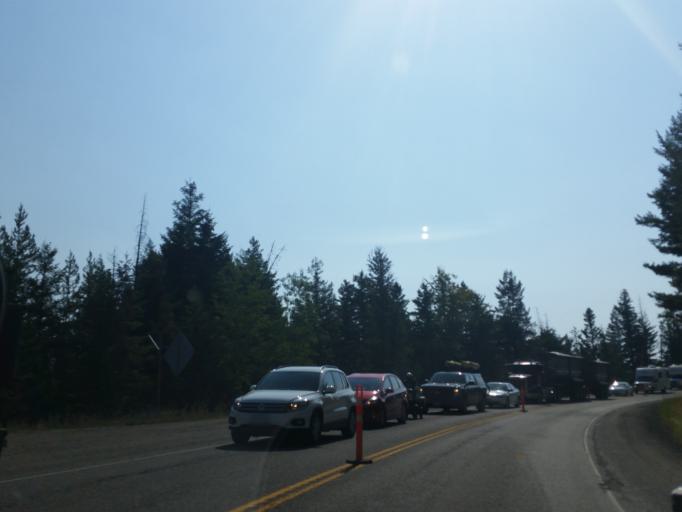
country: CA
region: British Columbia
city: Princeton
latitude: 49.2777
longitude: -120.5765
